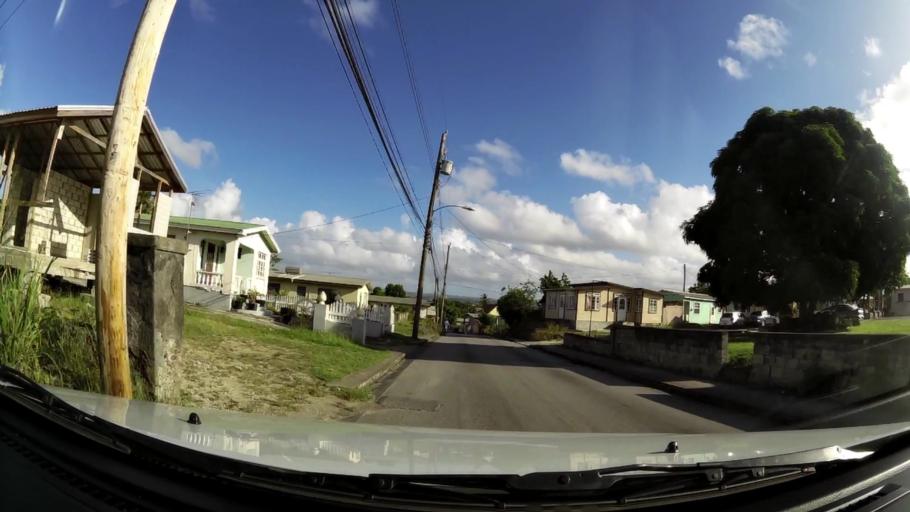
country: BB
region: Saint Michael
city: Bridgetown
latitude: 13.1061
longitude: -59.5898
